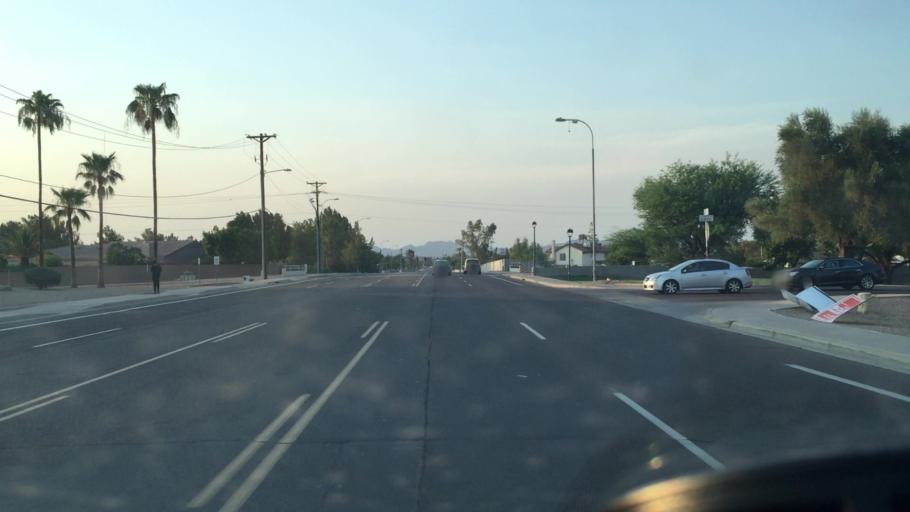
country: US
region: Arizona
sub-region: Maricopa County
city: Guadalupe
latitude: 33.3821
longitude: -111.9955
